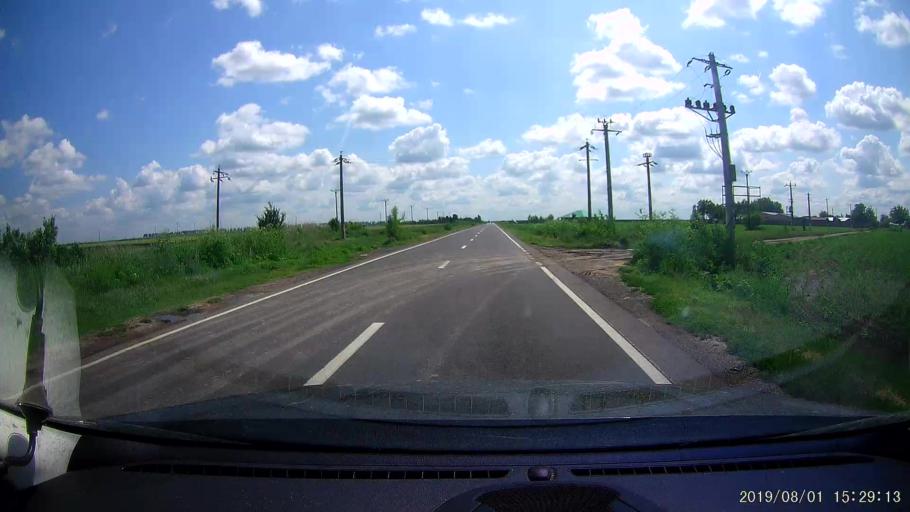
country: RO
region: Braila
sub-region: Comuna Viziru
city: Viziru
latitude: 44.9857
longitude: 27.7008
